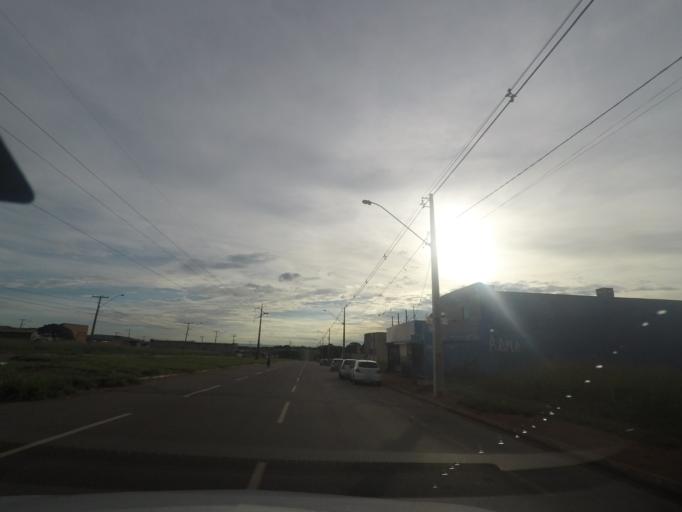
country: BR
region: Goias
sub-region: Trindade
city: Trindade
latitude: -16.7199
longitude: -49.3951
